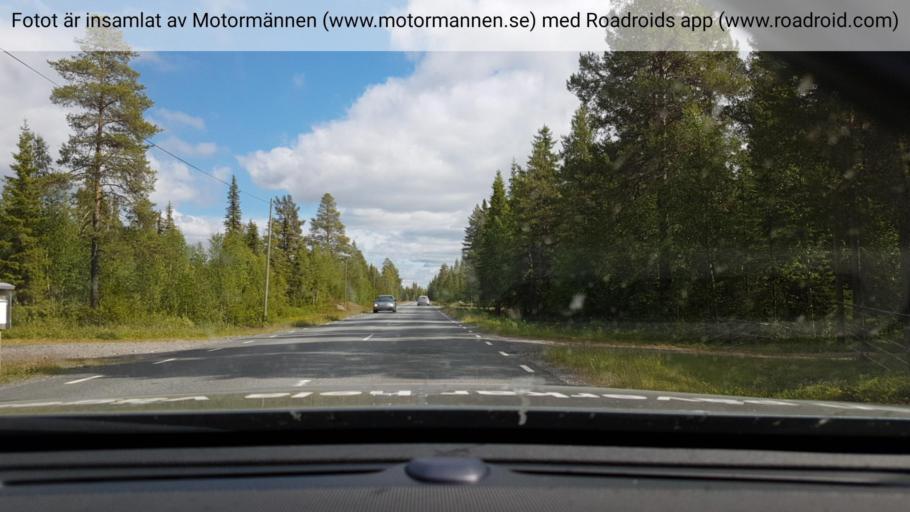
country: SE
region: Vaesterbotten
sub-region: Sorsele Kommun
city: Sorsele
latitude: 65.6660
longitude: 17.3985
